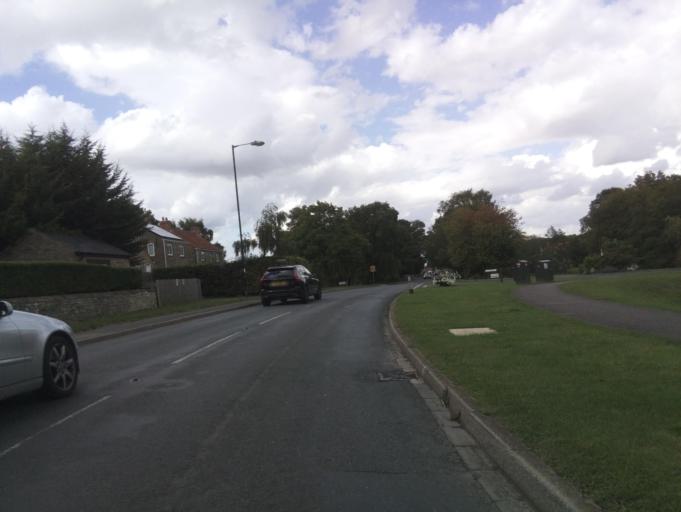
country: GB
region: England
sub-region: North Yorkshire
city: Ripon
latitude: 54.1867
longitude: -1.5628
